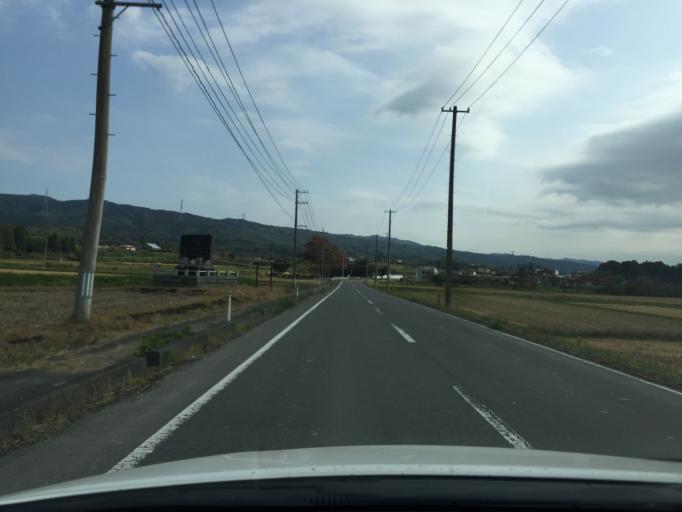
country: JP
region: Fukushima
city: Ishikawa
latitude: 36.9750
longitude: 140.4293
